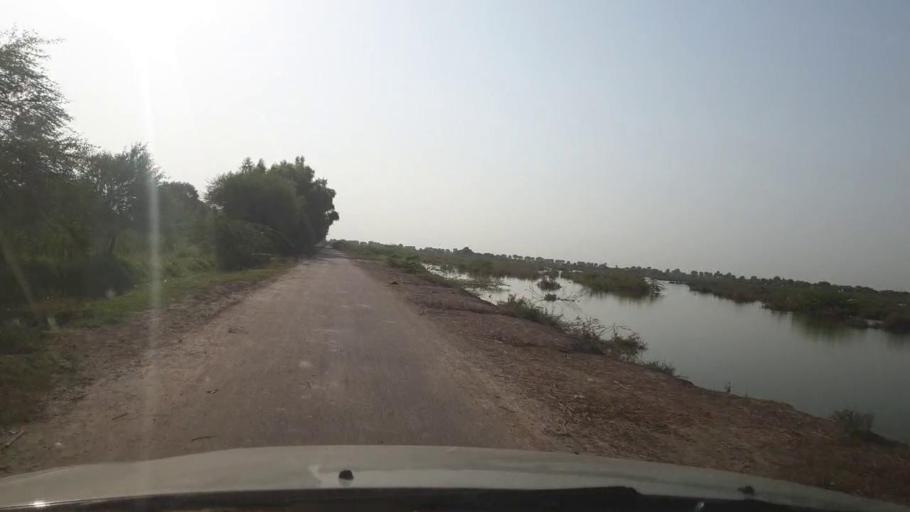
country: PK
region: Sindh
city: Tando Ghulam Ali
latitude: 25.1893
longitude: 68.9390
